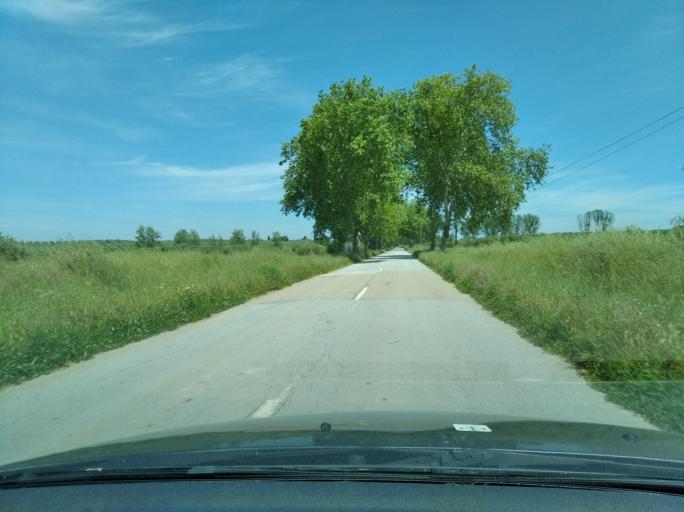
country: PT
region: Portalegre
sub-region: Avis
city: Avis
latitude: 39.0810
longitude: -7.8802
